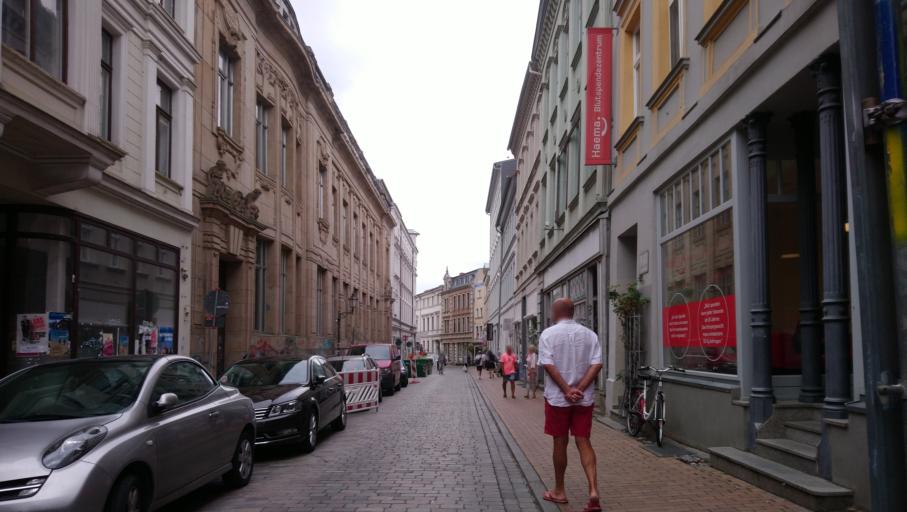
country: DE
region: Mecklenburg-Vorpommern
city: Schwerin
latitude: 53.6302
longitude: 11.4152
